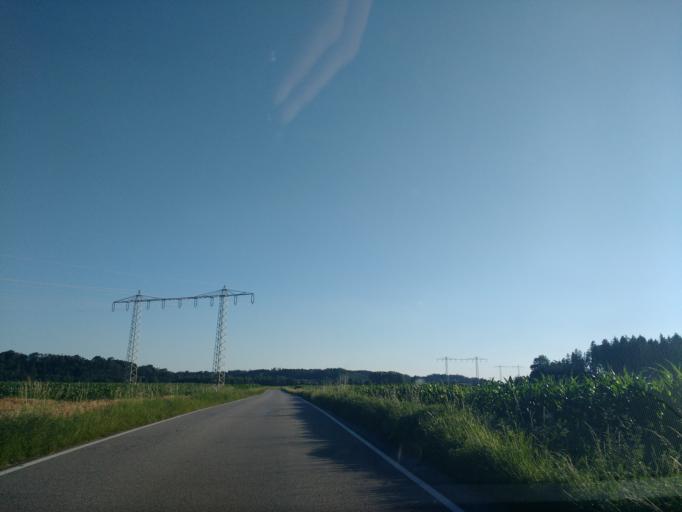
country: DE
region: Bavaria
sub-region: Upper Bavaria
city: Oberneukirchen
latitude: 48.2093
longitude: 12.5020
